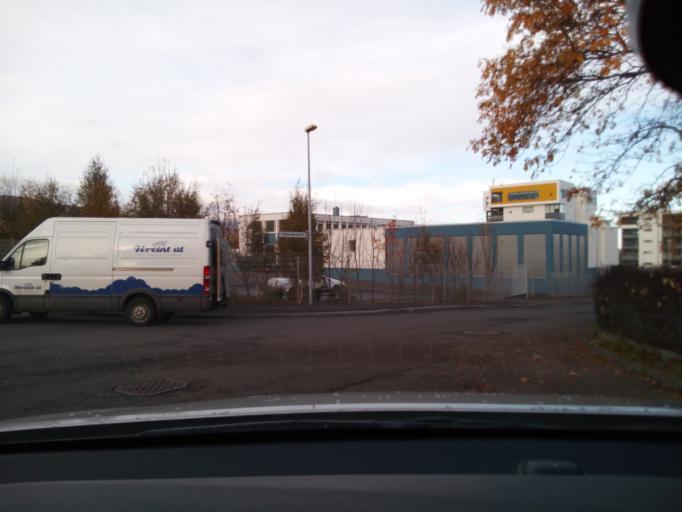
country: IS
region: Northeast
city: Akureyri
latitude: 65.6851
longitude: -18.0987
